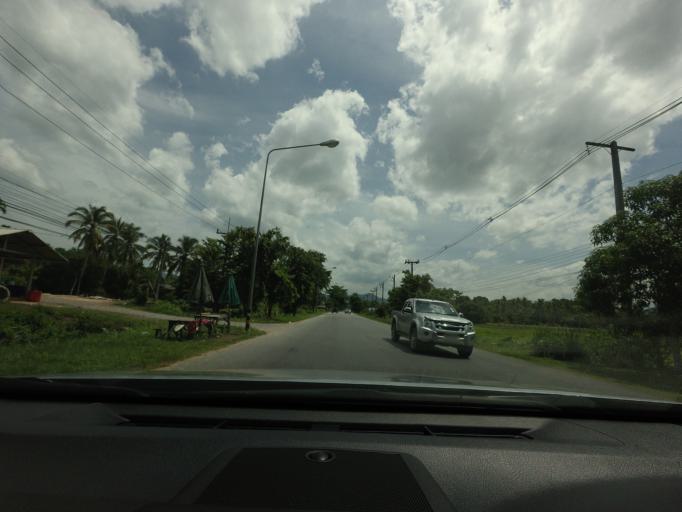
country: TH
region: Yala
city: Raman
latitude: 6.4640
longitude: 101.3796
